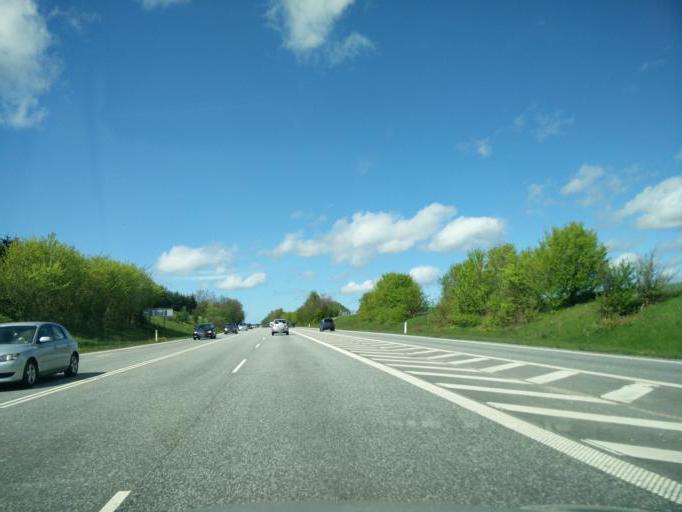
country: DK
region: Capital Region
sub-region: Hillerod Kommune
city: Hillerod
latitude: 55.9108
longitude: 12.2664
